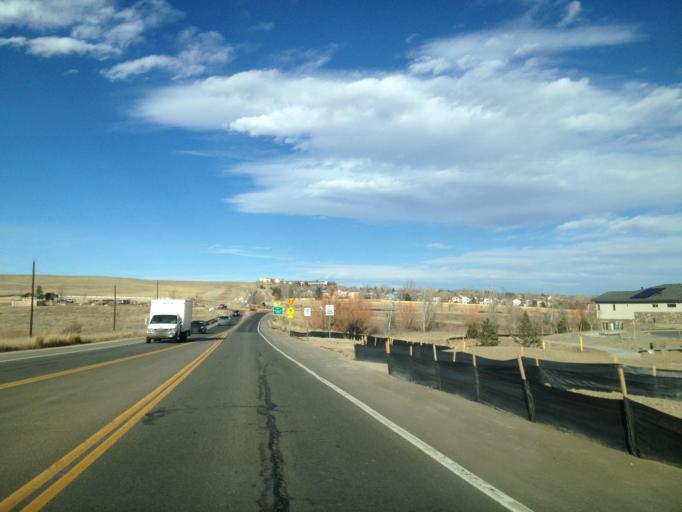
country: US
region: Colorado
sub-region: Boulder County
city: Superior
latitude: 39.9265
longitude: -105.1658
